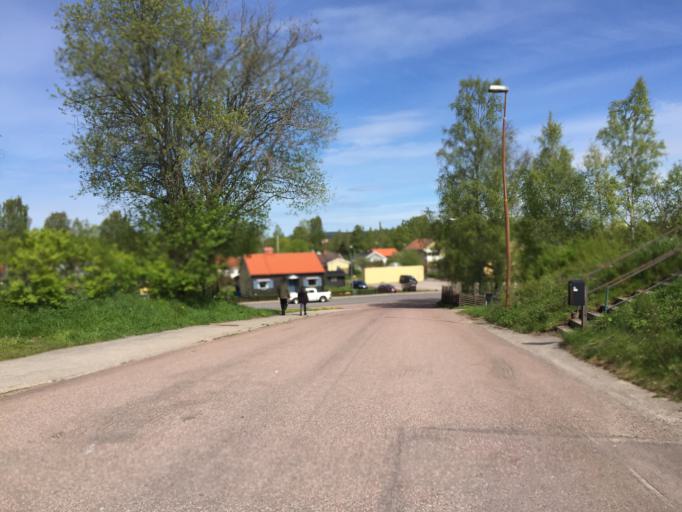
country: SE
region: Dalarna
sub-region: Ludvika Kommun
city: Ludvika
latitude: 60.1326
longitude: 15.1702
